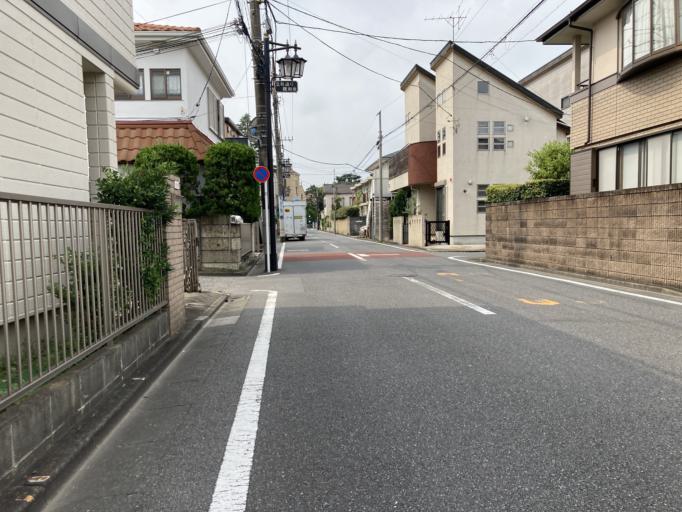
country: JP
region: Tokyo
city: Musashino
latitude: 35.6958
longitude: 139.5905
